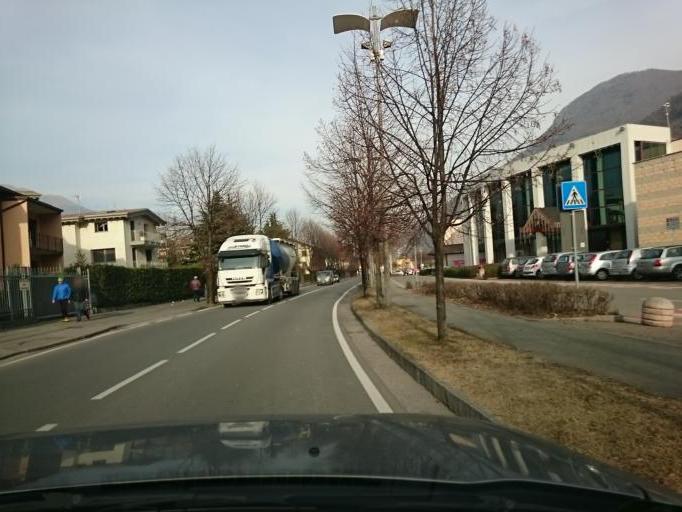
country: IT
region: Lombardy
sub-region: Provincia di Brescia
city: Pisogne
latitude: 45.8072
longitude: 10.1063
